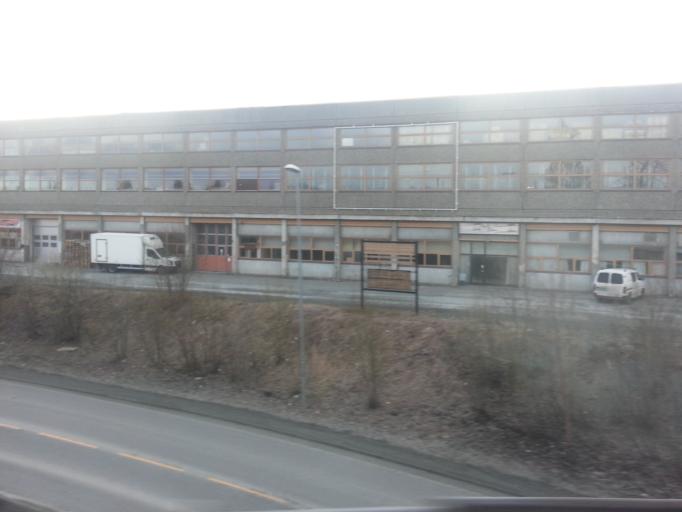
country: NO
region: Sor-Trondelag
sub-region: Trondheim
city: Trondheim
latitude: 63.3541
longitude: 10.3583
